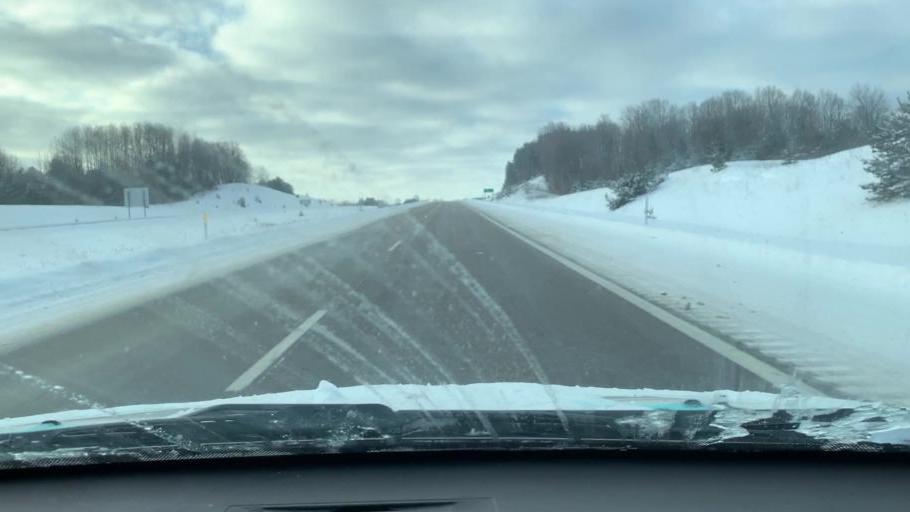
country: US
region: Michigan
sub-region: Wexford County
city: Manton
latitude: 44.3946
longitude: -85.3825
